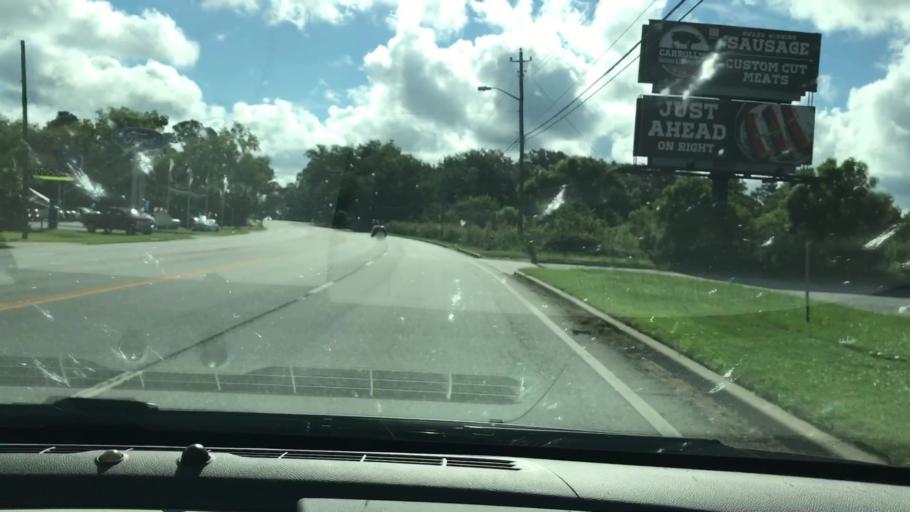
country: US
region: Georgia
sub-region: Worth County
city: Sylvester
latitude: 31.5316
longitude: -83.8513
